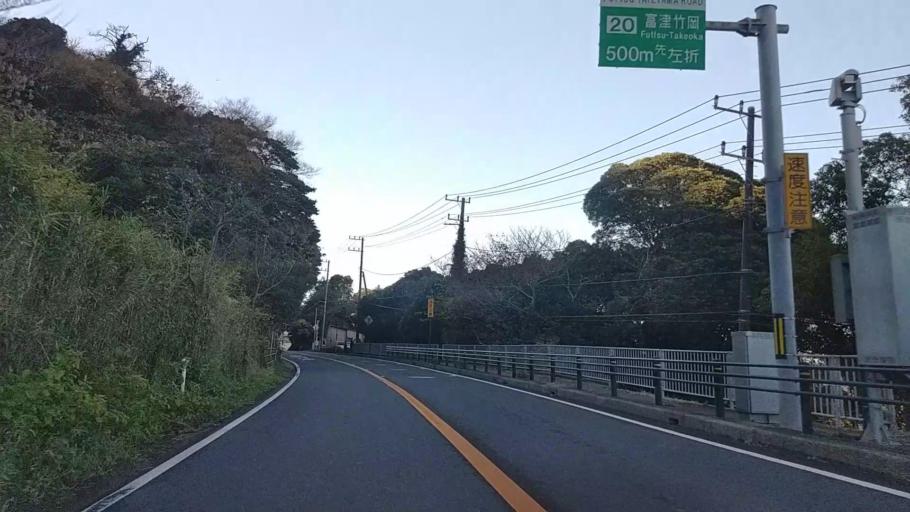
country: JP
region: Chiba
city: Futtsu
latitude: 35.2118
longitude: 139.8481
